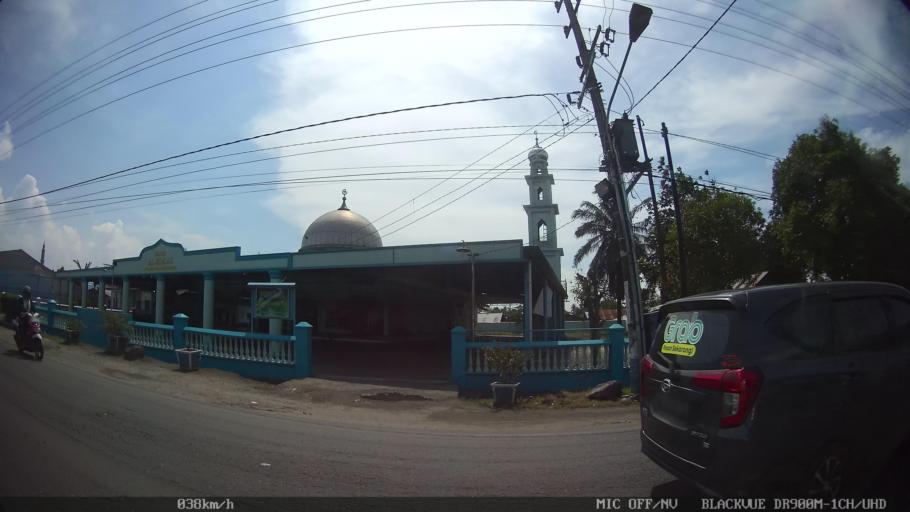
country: ID
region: North Sumatra
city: Labuhan Deli
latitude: 3.6595
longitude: 98.6565
